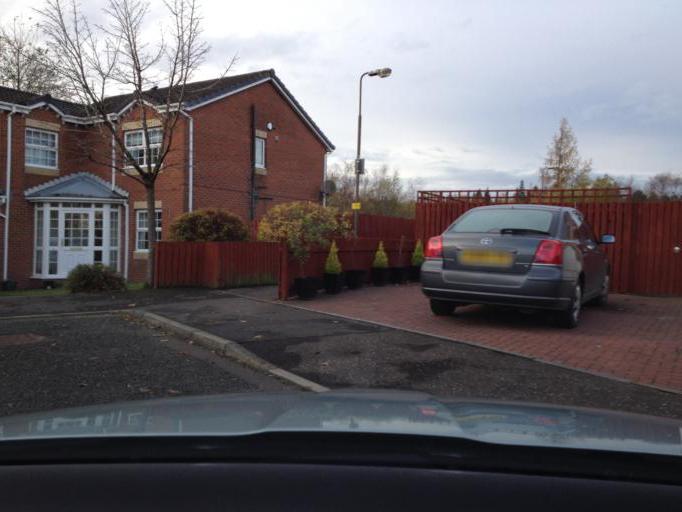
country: GB
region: Scotland
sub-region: West Lothian
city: Livingston
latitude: 55.8923
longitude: -3.5458
